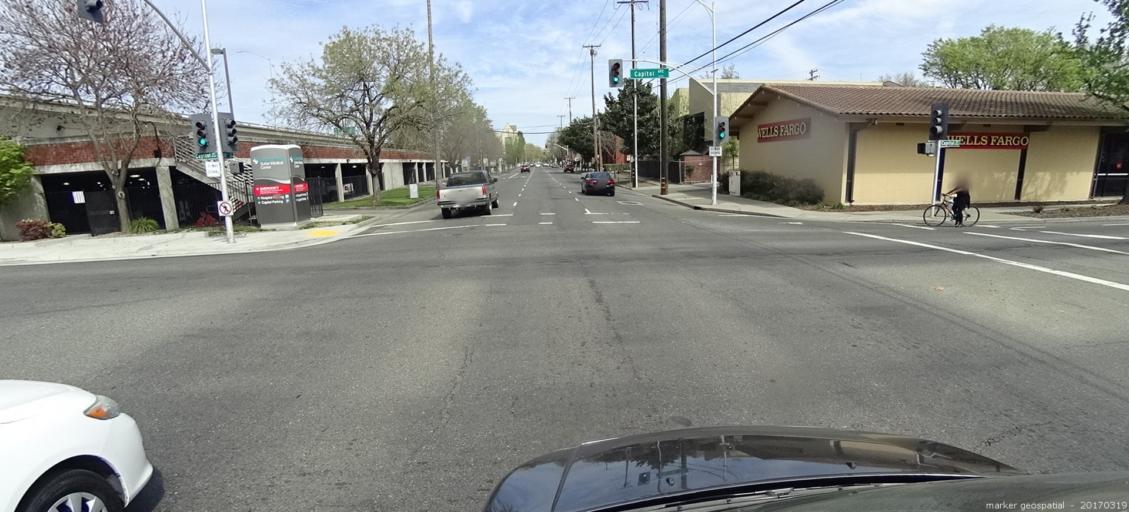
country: US
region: California
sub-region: Sacramento County
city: Sacramento
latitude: 38.5697
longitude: -121.4681
